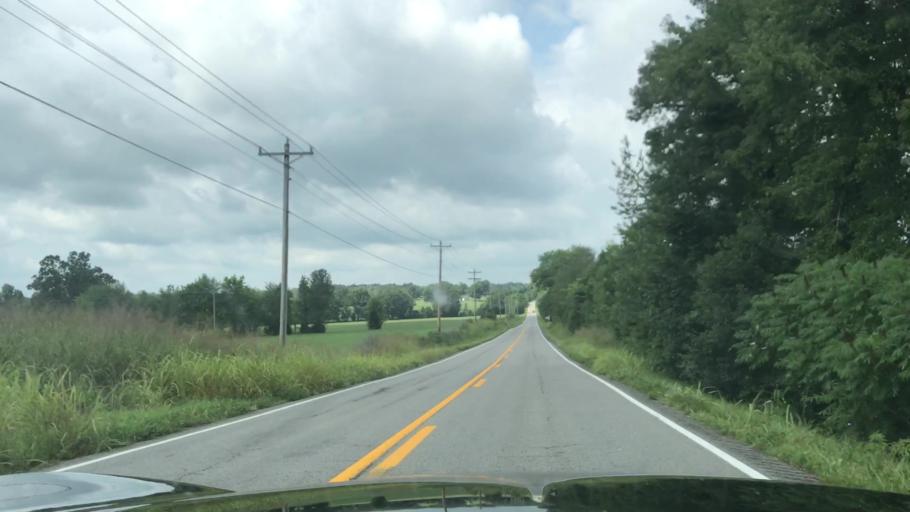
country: US
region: Kentucky
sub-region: Muhlenberg County
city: Central City
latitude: 37.1981
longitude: -86.9772
